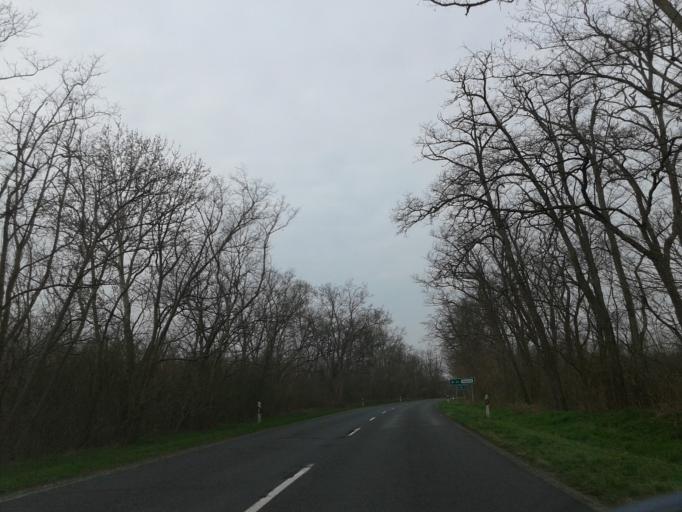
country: HU
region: Gyor-Moson-Sopron
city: Bony
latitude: 47.7338
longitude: 17.9048
